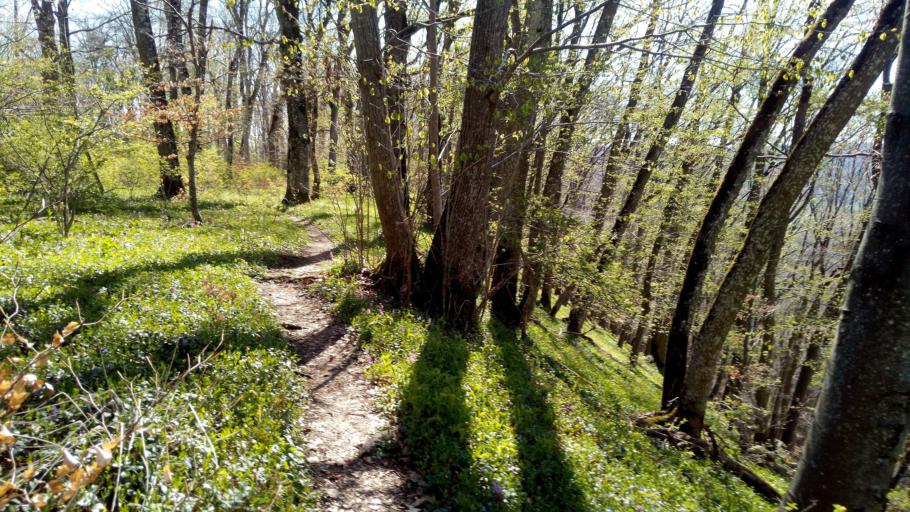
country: DE
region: Baden-Wuerttemberg
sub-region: Regierungsbezirk Stuttgart
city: Donzdorf
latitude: 48.7144
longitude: 9.8387
